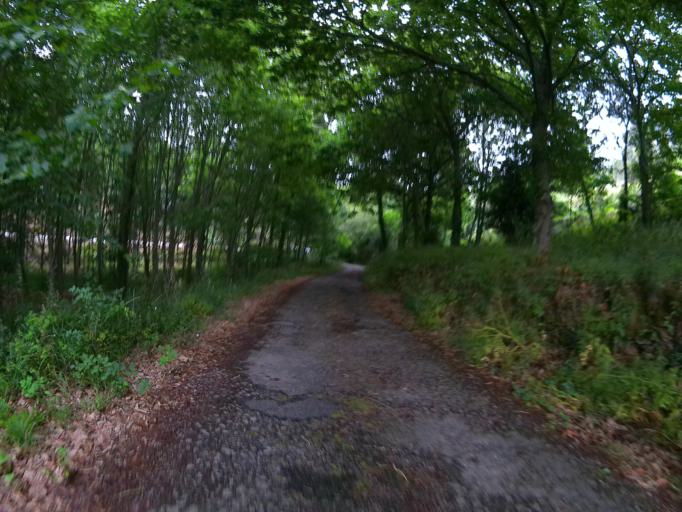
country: PT
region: Aveiro
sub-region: Albergaria-A-Velha
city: Branca
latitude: 40.7418
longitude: -8.4433
